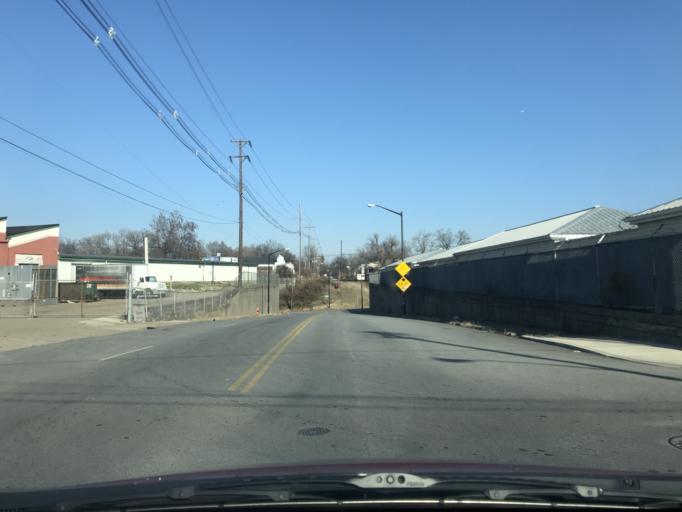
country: US
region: Kentucky
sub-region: Jefferson County
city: Louisville
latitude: 38.2238
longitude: -85.7535
